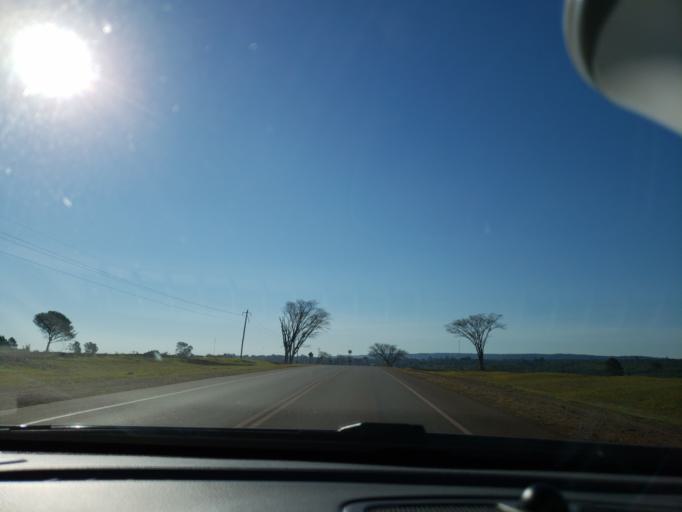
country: AR
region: Misiones
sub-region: Departamento de Apostoles
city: San Jose
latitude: -27.7881
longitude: -55.7719
